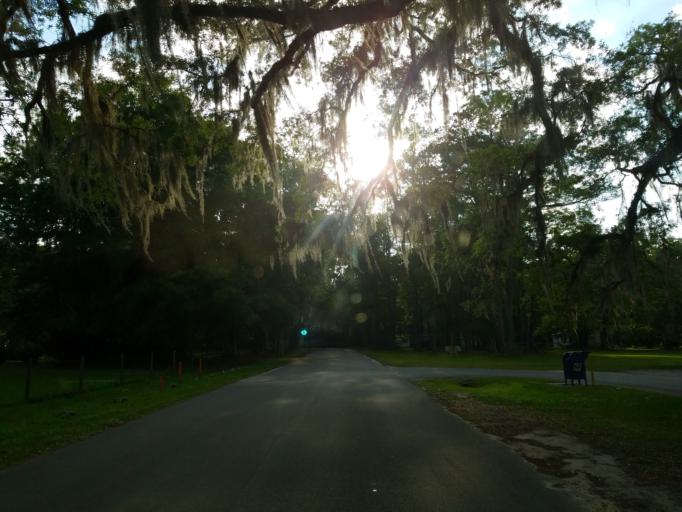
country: US
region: Florida
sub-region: Alachua County
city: Gainesville
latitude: 29.5080
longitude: -82.2805
